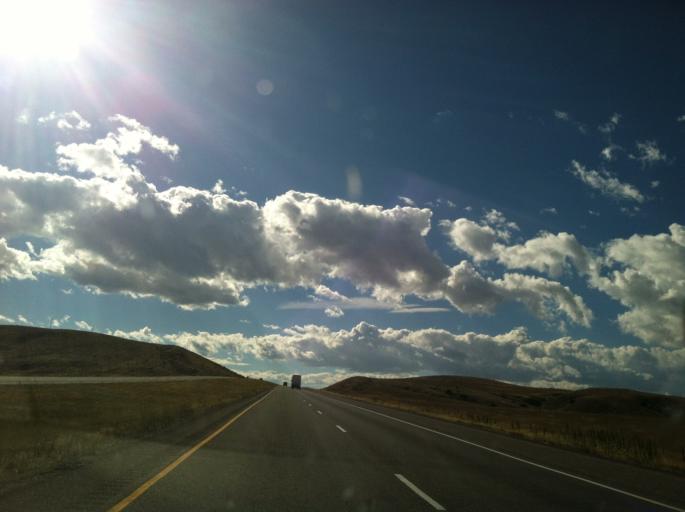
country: US
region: Montana
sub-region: Gallatin County
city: Three Forks
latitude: 45.9199
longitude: -111.6624
